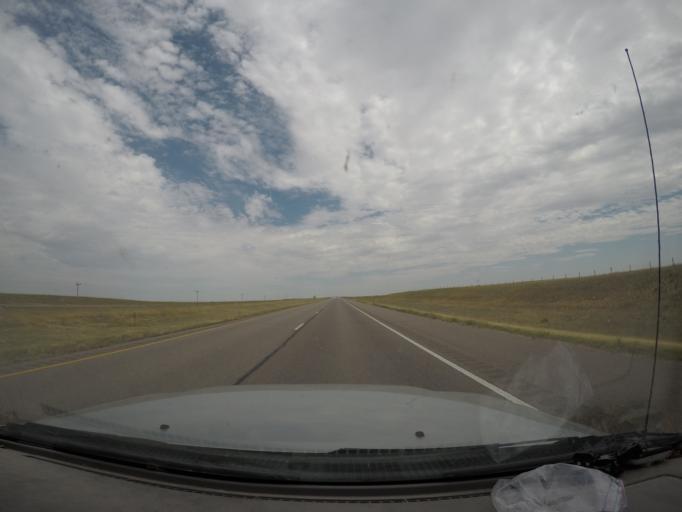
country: US
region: Nebraska
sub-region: Kimball County
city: Kimball
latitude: 41.1980
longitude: -103.7470
